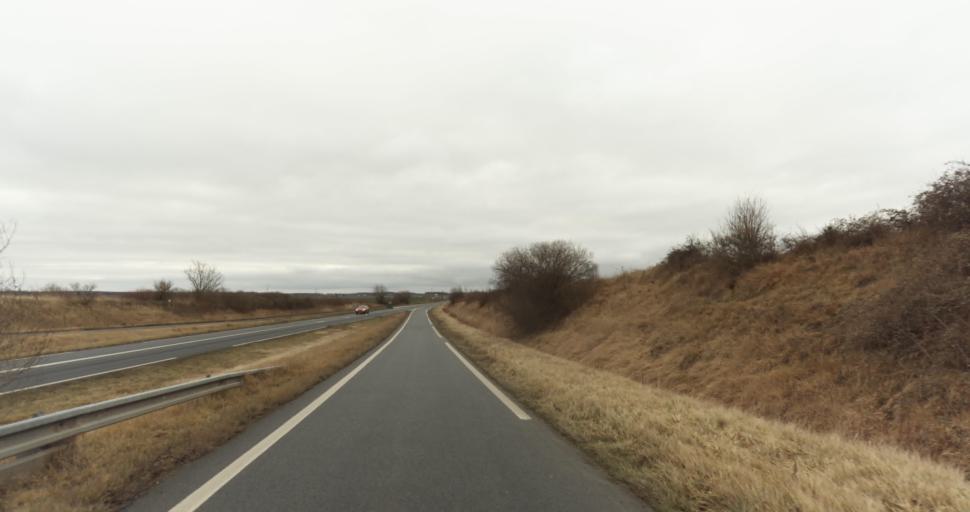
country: FR
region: Pays de la Loire
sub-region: Departement de Maine-et-Loire
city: Doue-la-Fontaine
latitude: 47.1961
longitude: -0.2452
